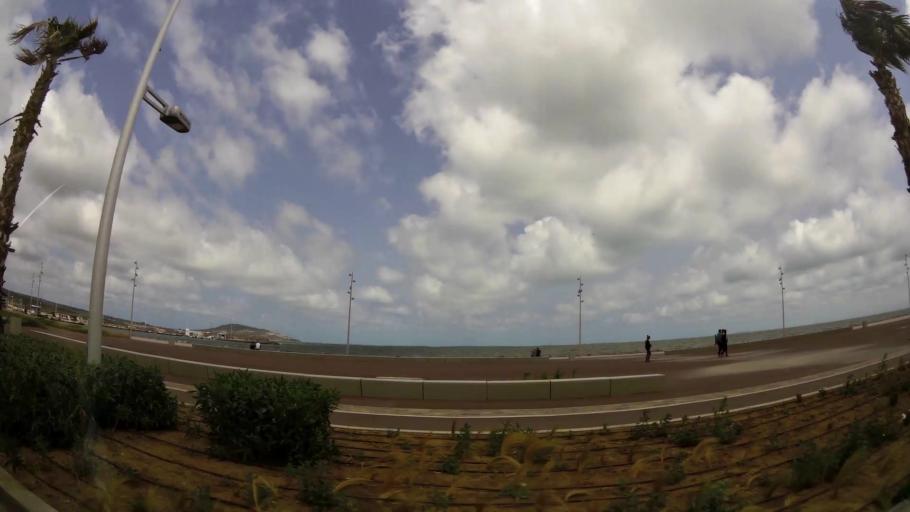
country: MA
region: Oriental
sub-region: Nador
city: Nador
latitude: 35.1836
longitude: -2.9245
